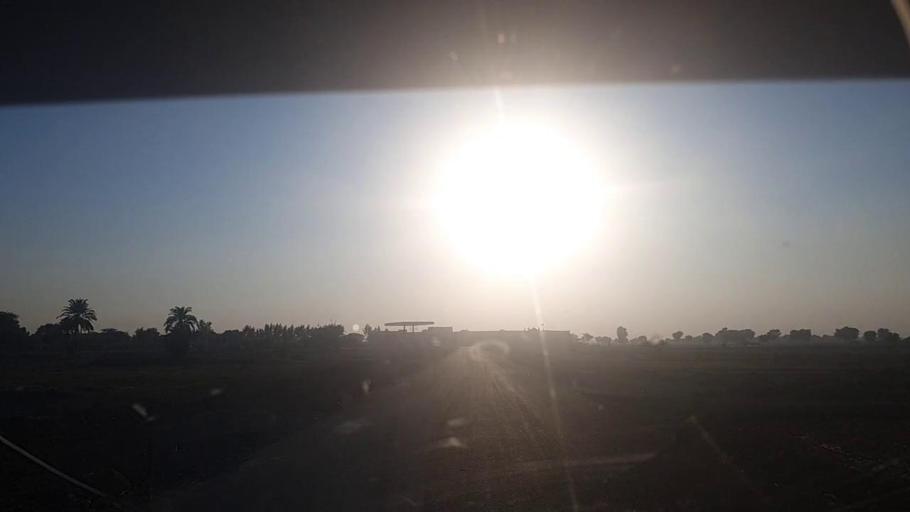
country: PK
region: Sindh
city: Hingorja
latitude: 27.2197
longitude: 68.4043
